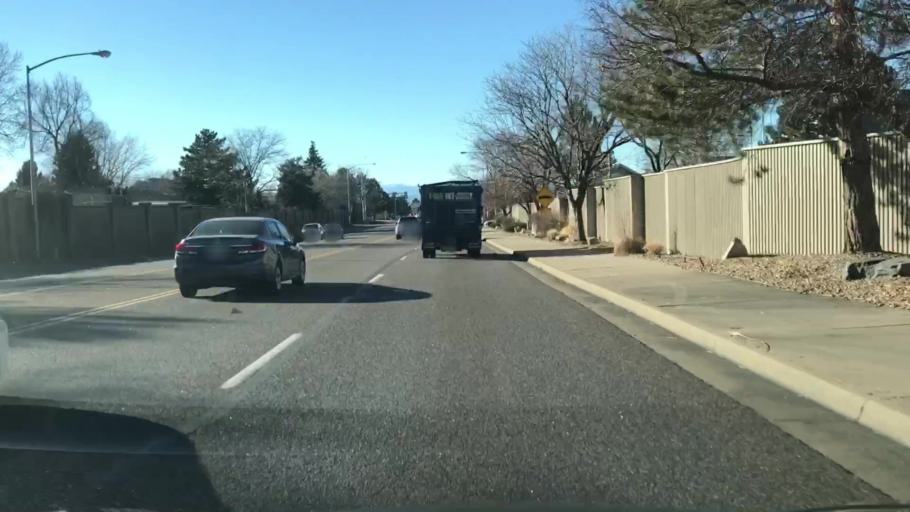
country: US
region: Colorado
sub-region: Adams County
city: Aurora
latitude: 39.6749
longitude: -104.8600
